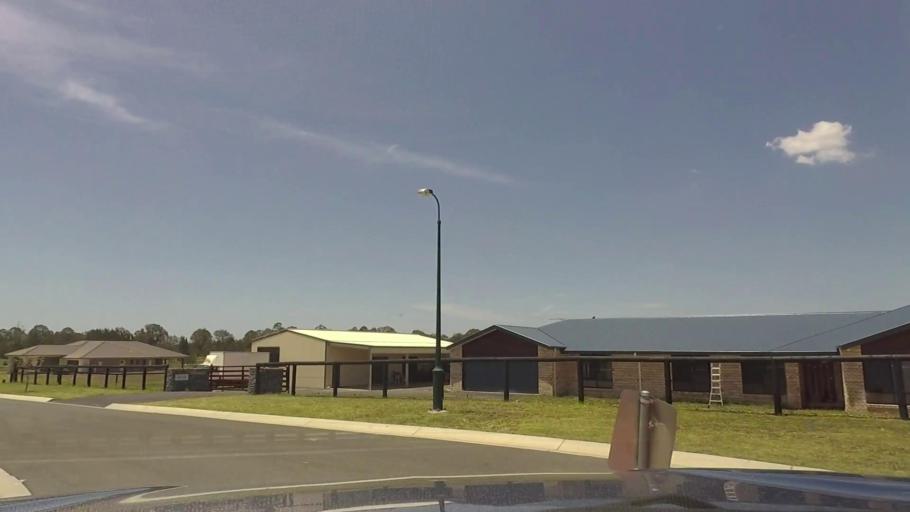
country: AU
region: Queensland
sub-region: Logan
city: Chambers Flat
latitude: -27.7743
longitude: 153.0931
